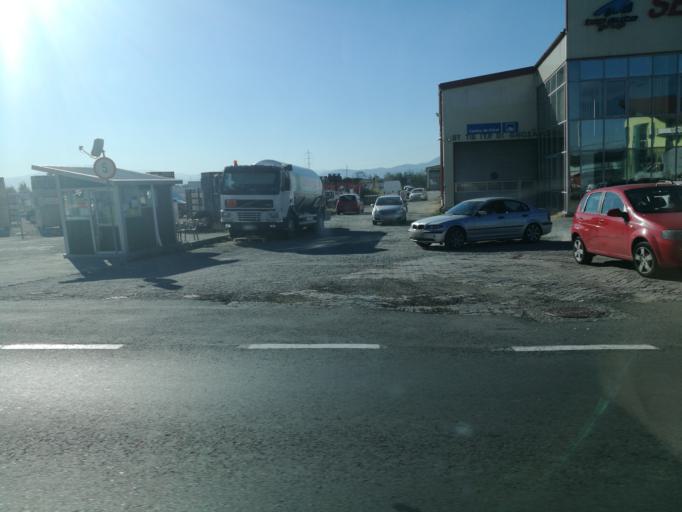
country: RO
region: Brasov
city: Brasov
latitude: 45.6917
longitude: 25.5836
